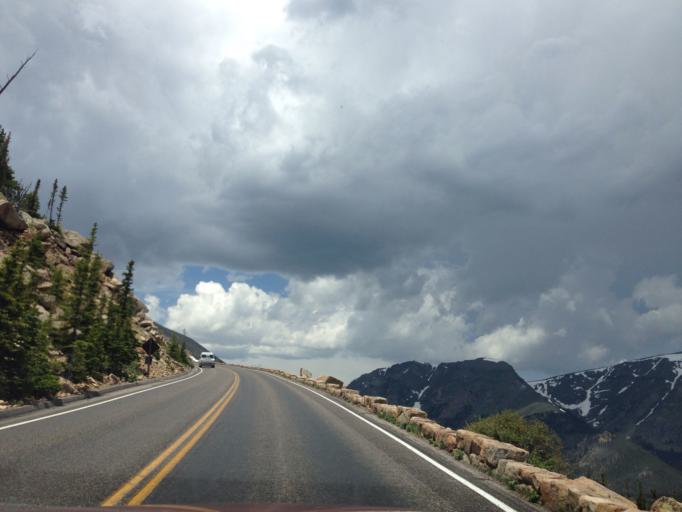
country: US
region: Colorado
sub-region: Larimer County
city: Estes Park
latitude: 40.4017
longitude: -105.6651
